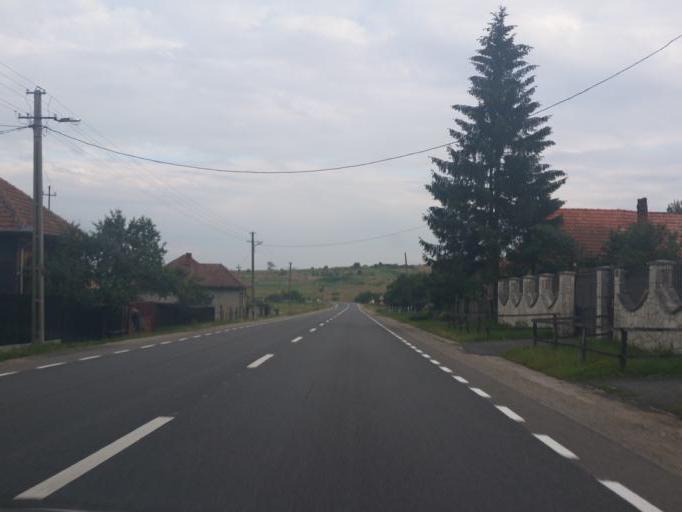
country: RO
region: Cluj
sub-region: Comuna Sanpaul
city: Sanpaul
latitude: 46.9301
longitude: 23.3967
